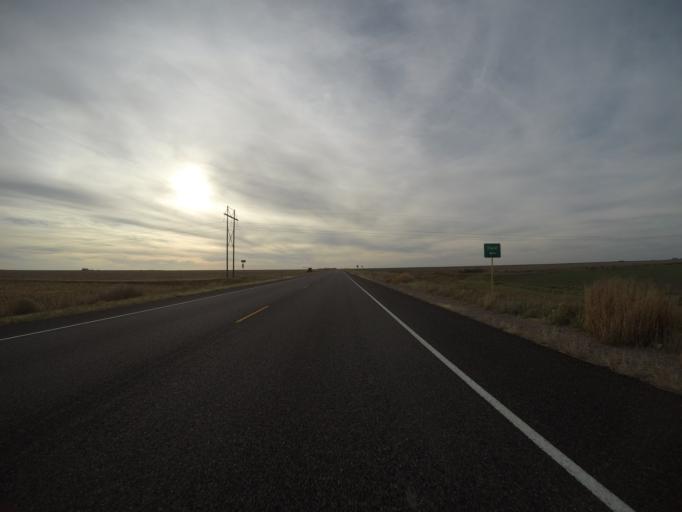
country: US
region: Colorado
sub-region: Yuma County
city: Wray
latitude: 39.7460
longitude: -102.1446
